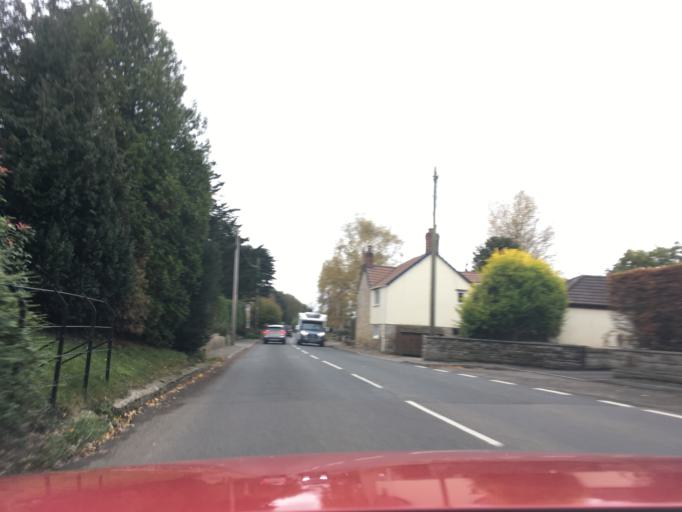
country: GB
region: England
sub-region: Somerset
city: Yeovil
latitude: 50.9997
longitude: -2.5840
